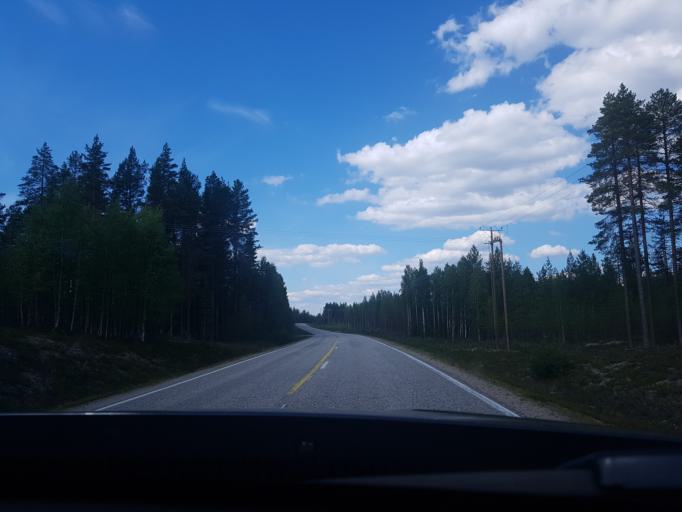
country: FI
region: Kainuu
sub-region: Kehys-Kainuu
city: Kuhmo
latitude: 64.2410
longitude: 29.8131
